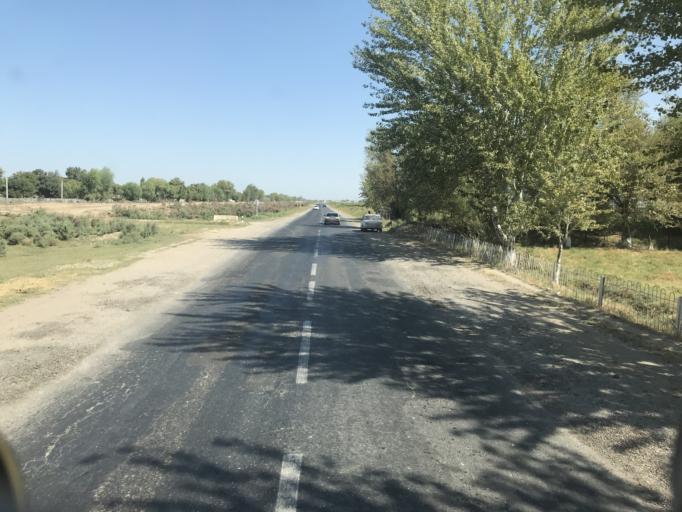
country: KZ
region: Ongtustik Qazaqstan
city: Ilyich
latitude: 40.7705
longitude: 68.5373
